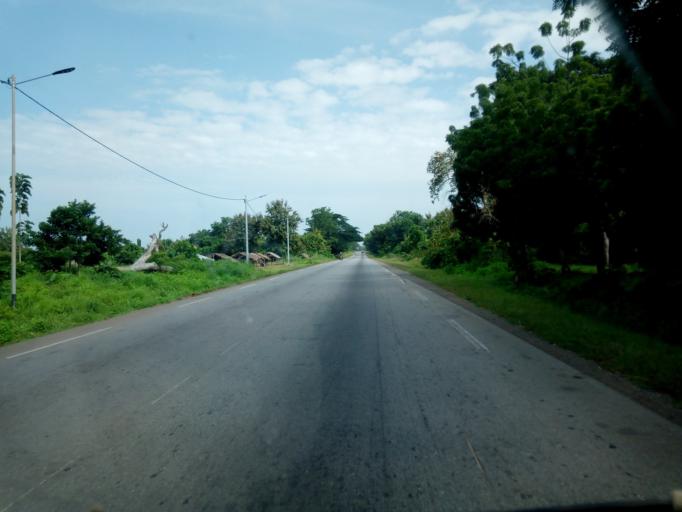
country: TG
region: Plateaux
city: Notse
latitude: 7.0483
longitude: 1.1559
